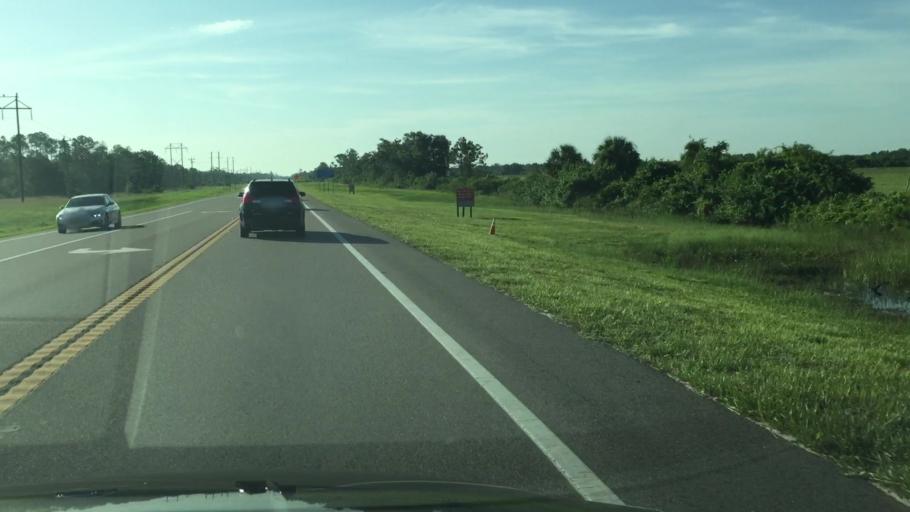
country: US
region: Florida
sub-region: Lee County
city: Gateway
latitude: 26.5662
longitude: -81.6766
